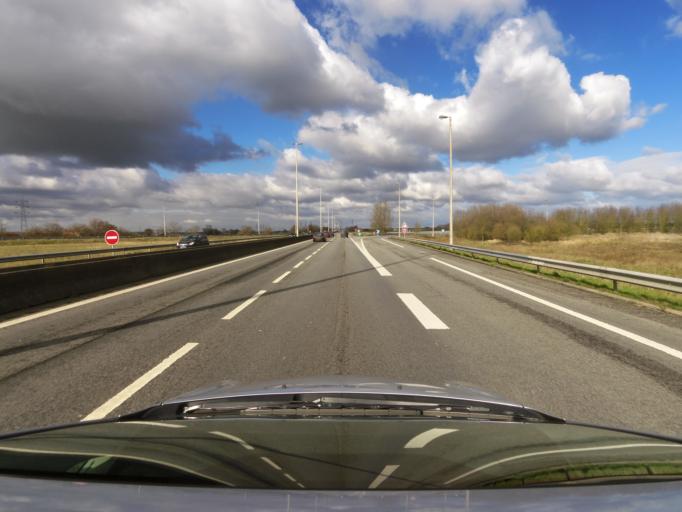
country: FR
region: Nord-Pas-de-Calais
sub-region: Departement du Nord
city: Bourbourg
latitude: 50.9589
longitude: 2.1847
